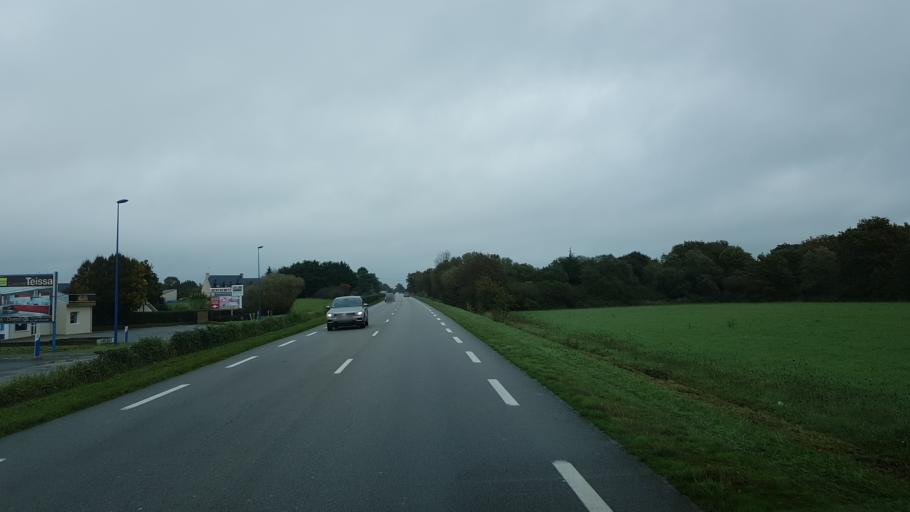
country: FR
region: Brittany
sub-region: Departement du Morbihan
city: Theix
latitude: 47.5856
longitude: -2.6895
